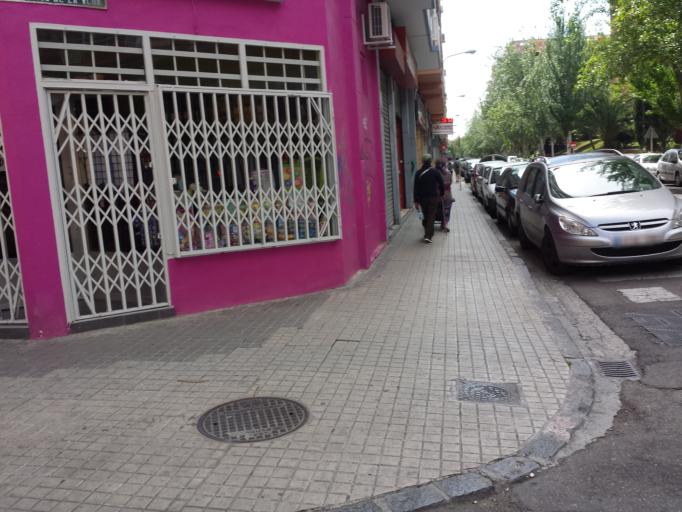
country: ES
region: Aragon
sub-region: Provincia de Zaragoza
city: Delicias
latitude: 41.6523
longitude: -0.9129
